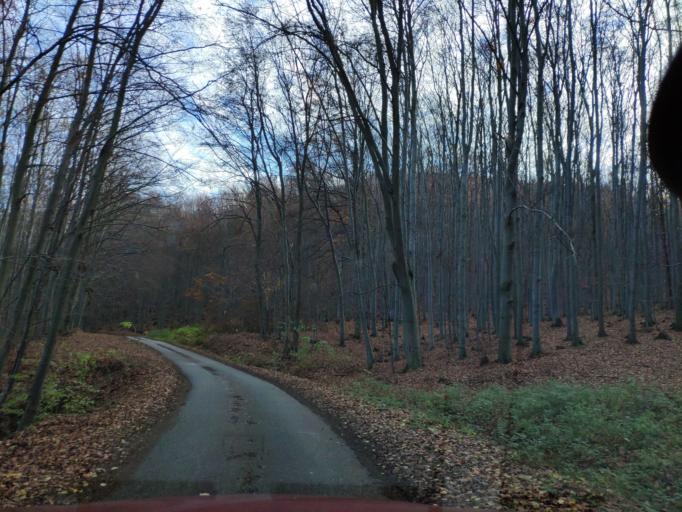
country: HU
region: Borsod-Abauj-Zemplen
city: Gonc
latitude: 48.5879
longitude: 21.4626
